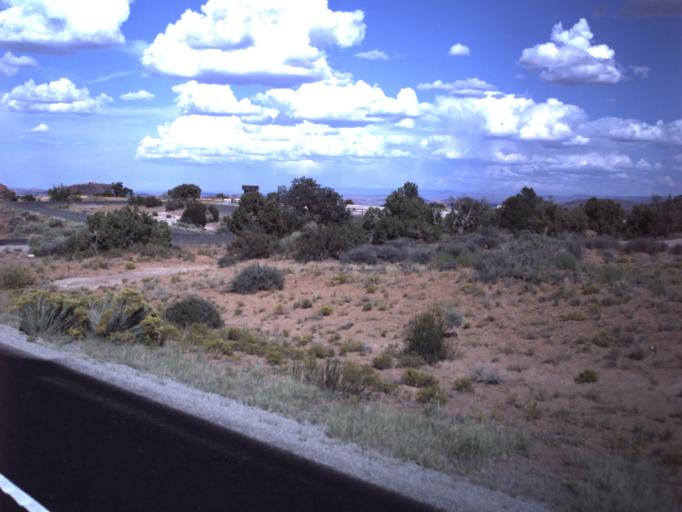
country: US
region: Utah
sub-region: Grand County
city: Moab
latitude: 38.6294
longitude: -109.8013
